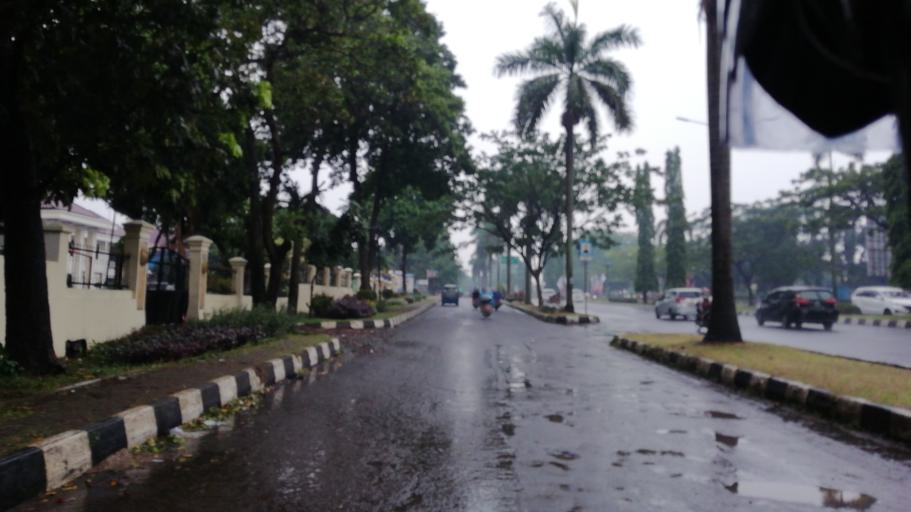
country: ID
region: West Java
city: Cibinong
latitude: -6.4843
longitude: 106.8352
